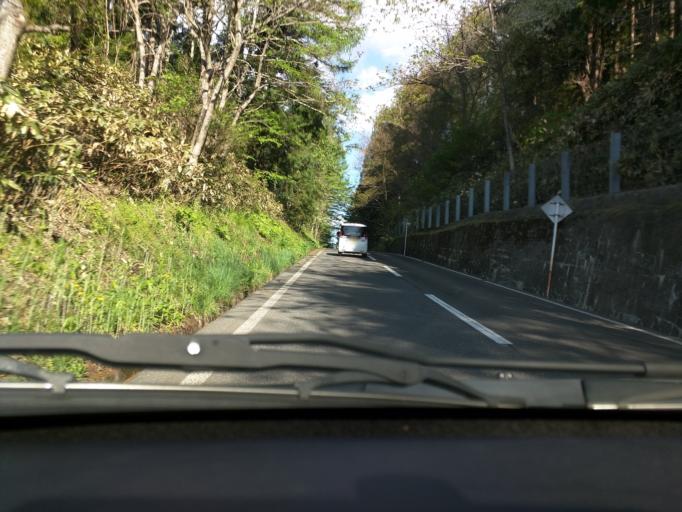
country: JP
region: Nagano
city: Nagano-shi
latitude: 36.6817
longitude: 138.1684
